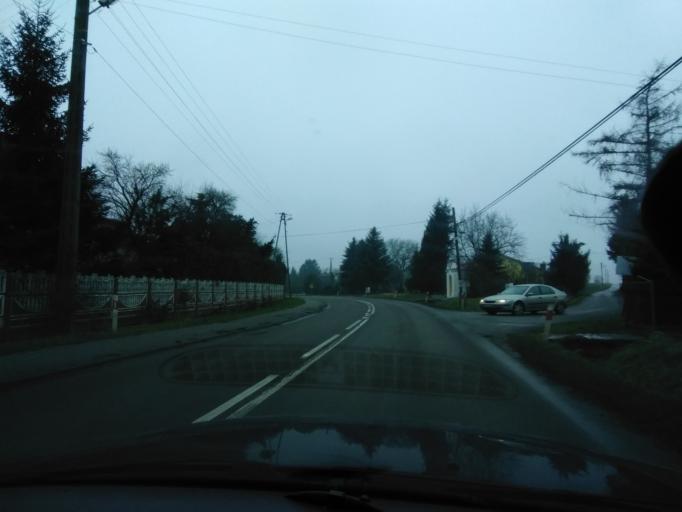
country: PL
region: Subcarpathian Voivodeship
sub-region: Powiat przeworski
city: Urzejowice
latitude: 50.0109
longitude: 22.4562
